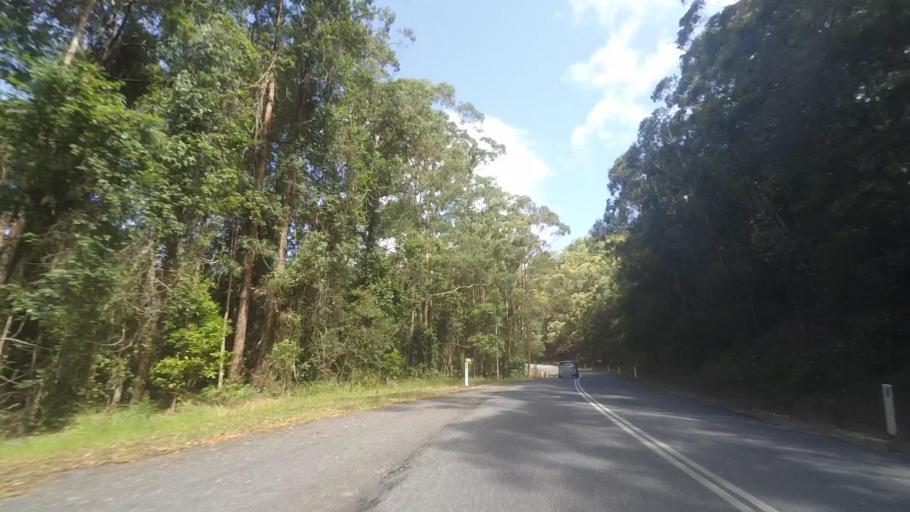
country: AU
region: New South Wales
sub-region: Great Lakes
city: Bulahdelah
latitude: -32.4023
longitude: 152.2957
